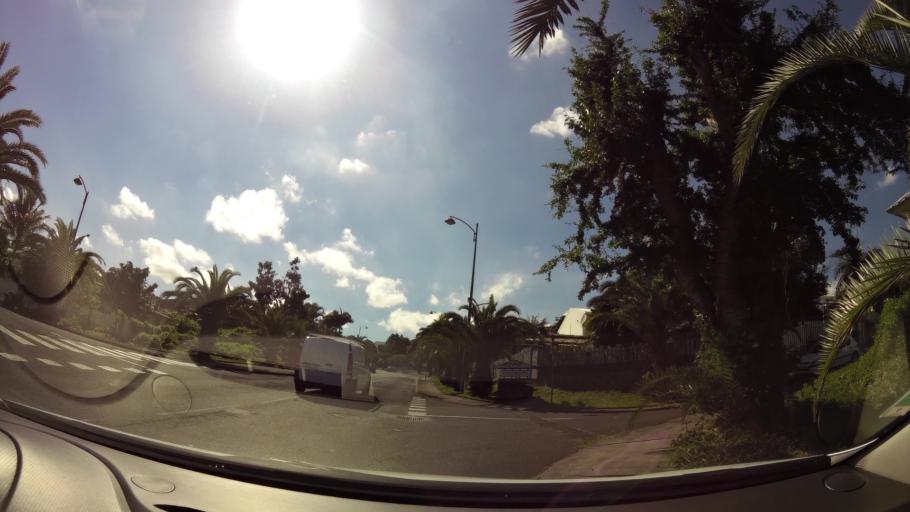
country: RE
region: Reunion
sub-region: Reunion
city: Le Tampon
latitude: -21.2798
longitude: 55.5019
